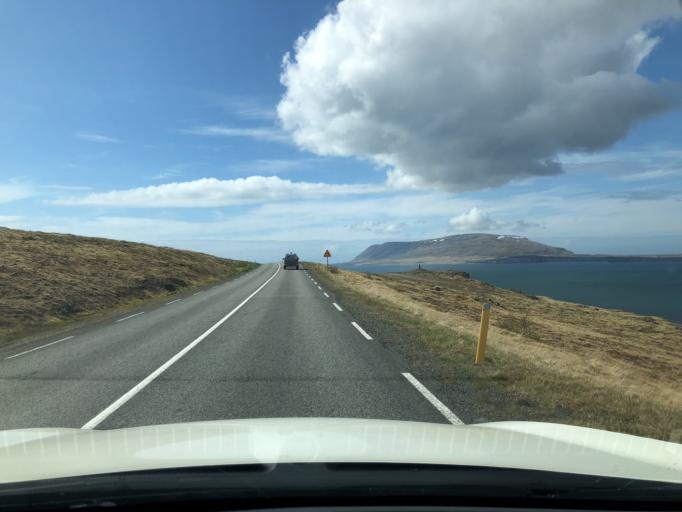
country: IS
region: Capital Region
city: Mosfellsbaer
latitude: 64.3585
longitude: -21.6354
